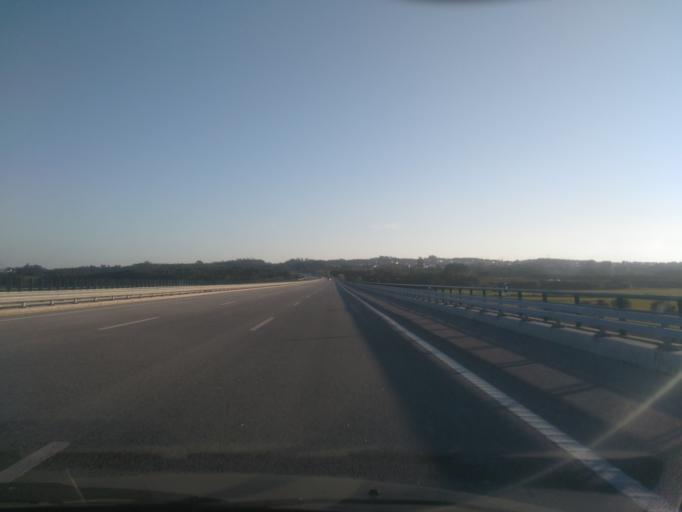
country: PT
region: Coimbra
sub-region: Figueira da Foz
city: Lavos
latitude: 40.0962
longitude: -8.7553
